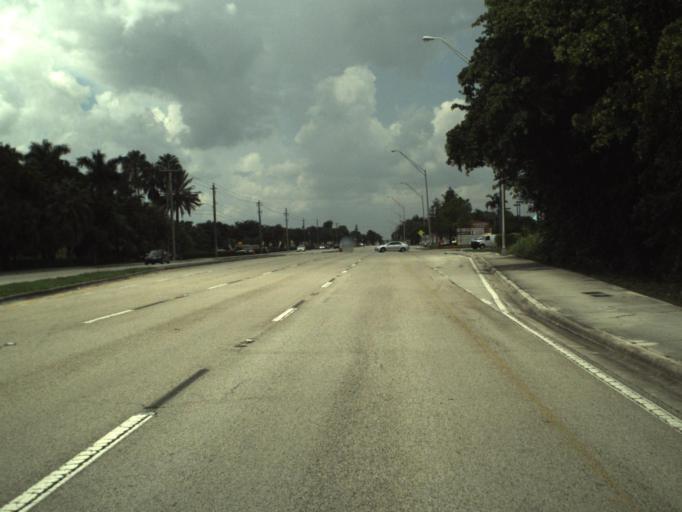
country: US
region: Florida
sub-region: Broward County
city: Davie
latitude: 26.0460
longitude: -80.2347
